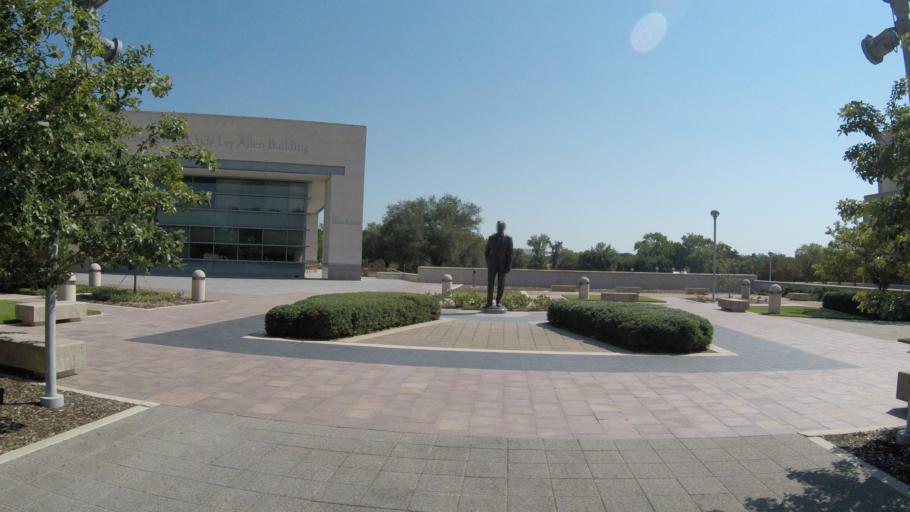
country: US
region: Texas
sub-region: Brazos County
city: College Station
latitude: 30.5970
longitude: -96.3530
